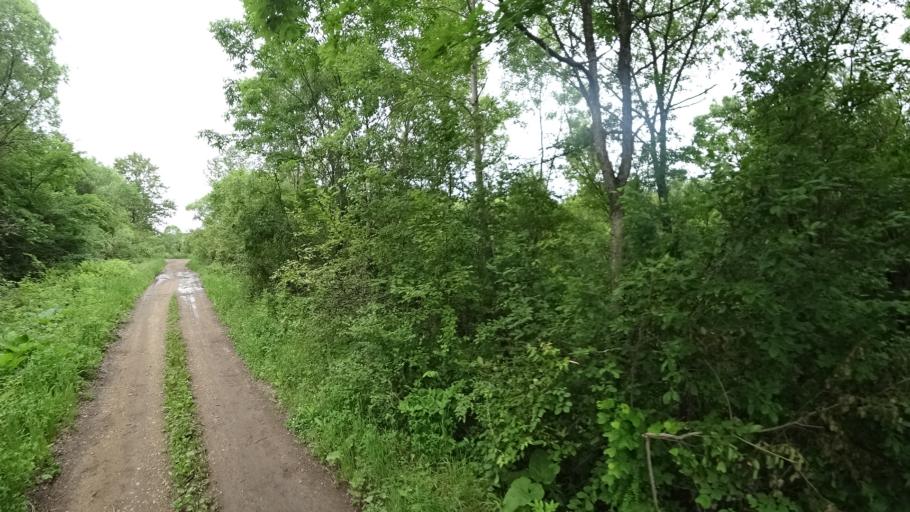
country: RU
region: Primorskiy
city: Novosysoyevka
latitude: 44.2041
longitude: 133.3265
